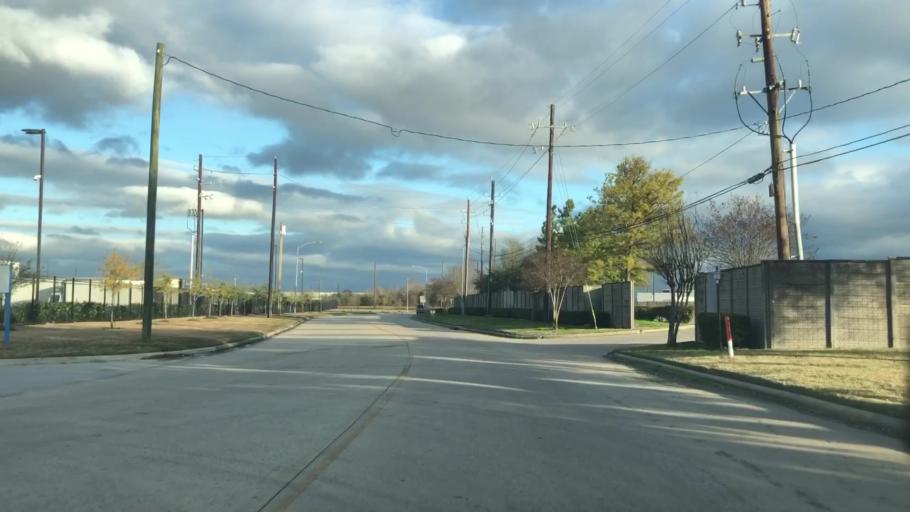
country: US
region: Texas
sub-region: Harris County
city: Aldine
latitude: 29.9159
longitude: -95.4164
